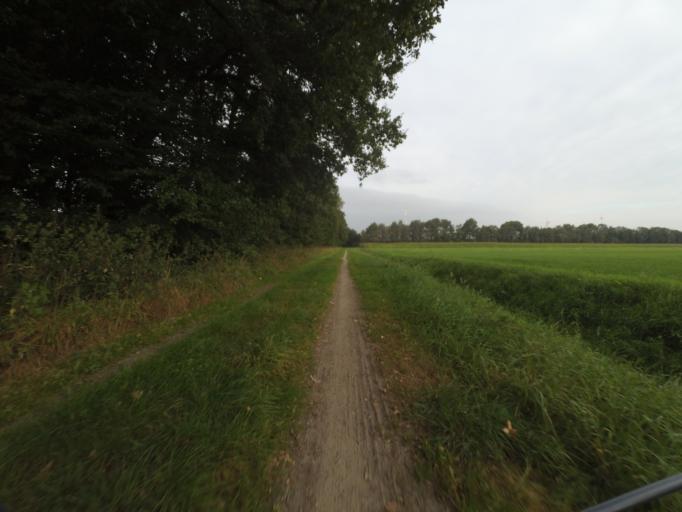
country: DE
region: Lower Saxony
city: Isterberg
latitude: 52.3156
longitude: 7.0812
